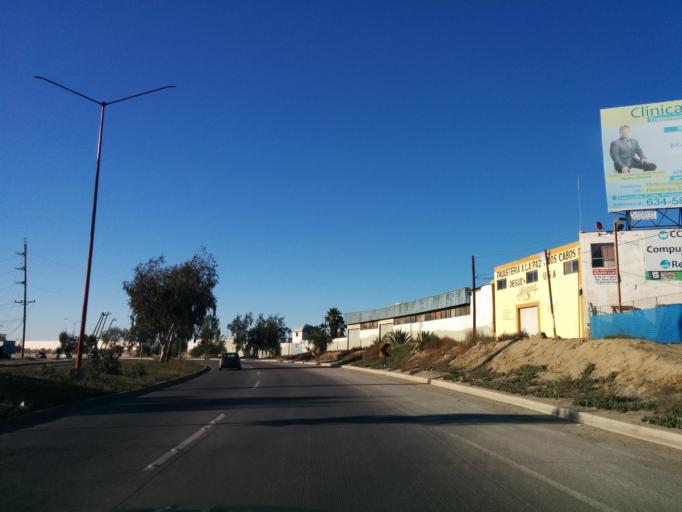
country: MX
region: Baja California
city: Tijuana
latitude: 32.5477
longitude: -116.9487
